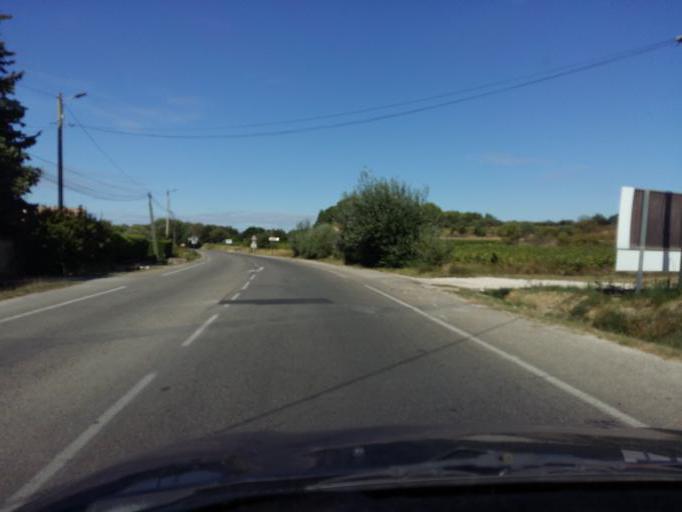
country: FR
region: Provence-Alpes-Cote d'Azur
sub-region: Departement du Vaucluse
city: Mazan
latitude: 44.0589
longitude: 5.1109
